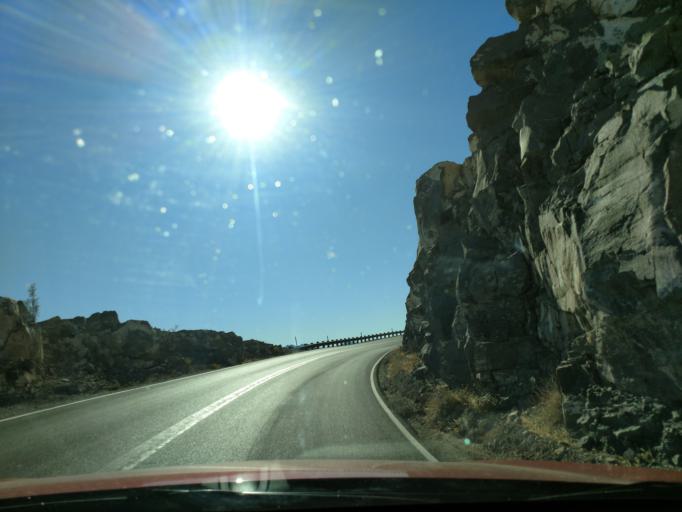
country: US
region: California
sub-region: Inyo County
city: Lone Pine
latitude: 36.3456
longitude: -117.5384
